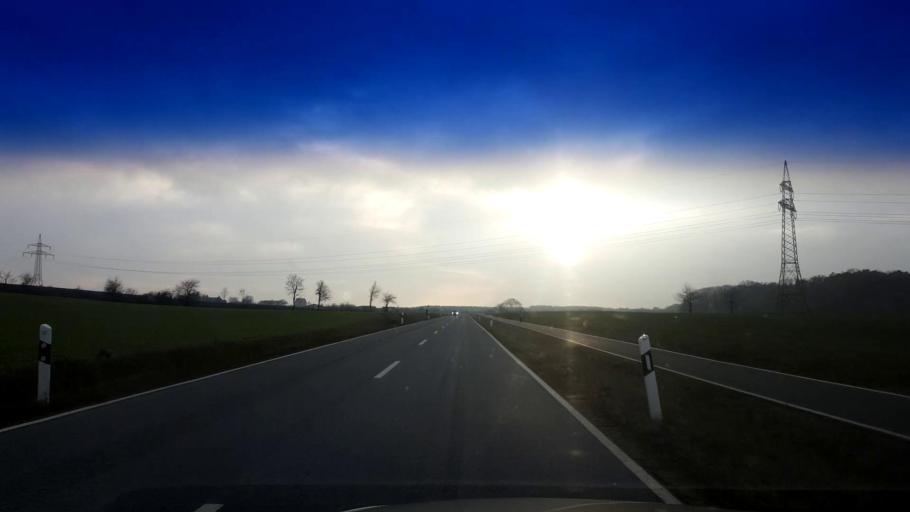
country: DE
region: Bavaria
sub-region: Upper Franconia
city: Hirschaid
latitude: 49.7925
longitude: 10.9624
